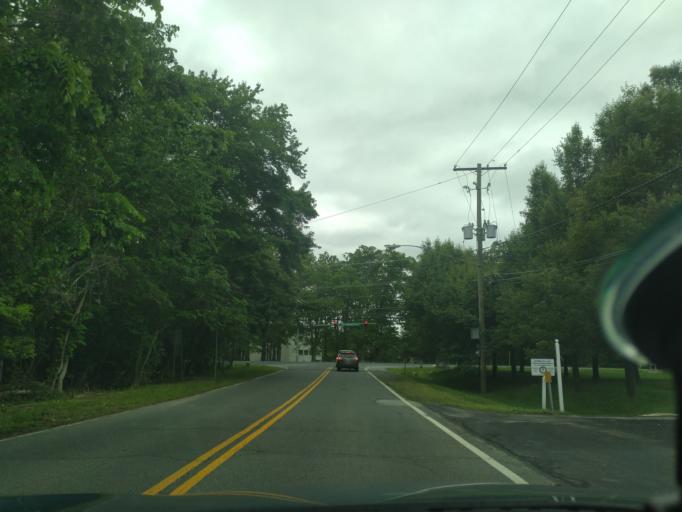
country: US
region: Maryland
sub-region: Prince George's County
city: Friendly
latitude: 38.7378
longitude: -77.0035
